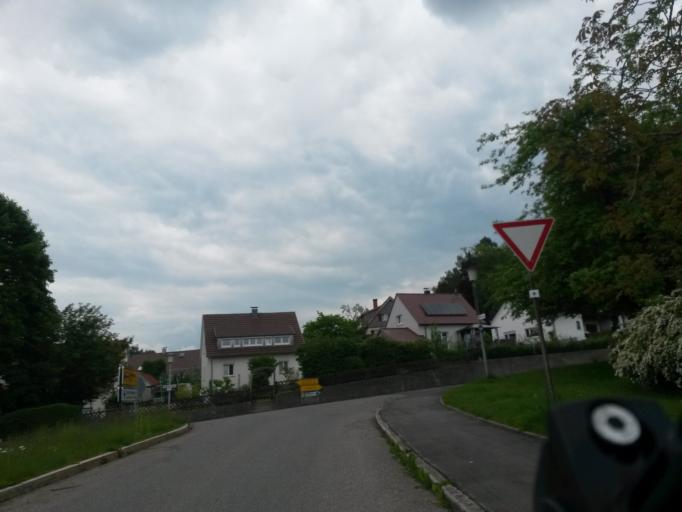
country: DE
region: Baden-Wuerttemberg
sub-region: Tuebingen Region
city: Wolfegg
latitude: 47.8402
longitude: 9.7898
